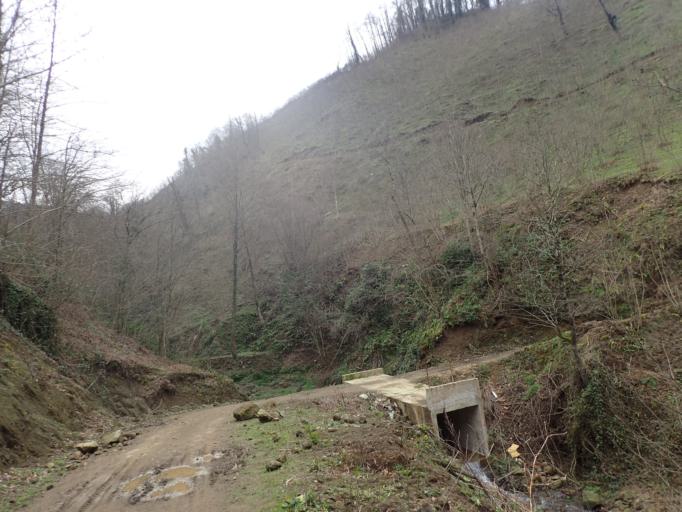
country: TR
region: Ordu
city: Camas
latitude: 40.8888
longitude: 37.5057
